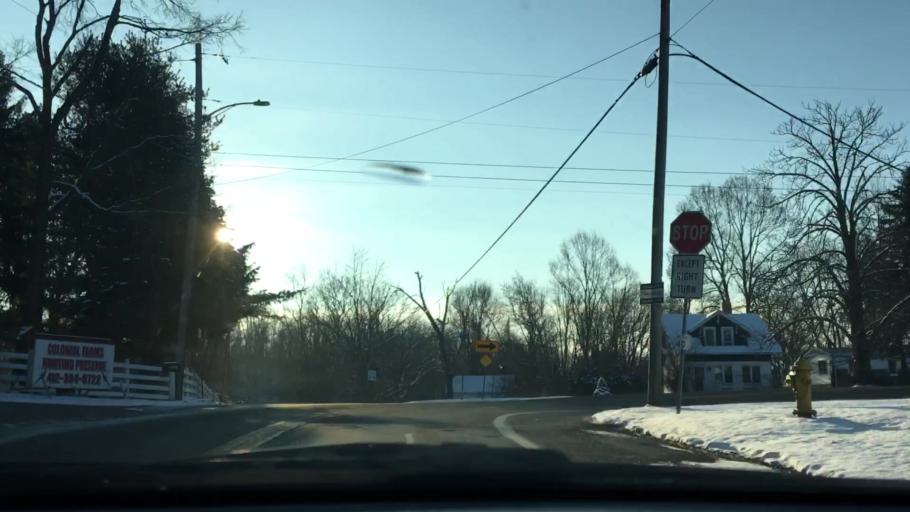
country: US
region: Pennsylvania
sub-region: Allegheny County
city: Elizabeth
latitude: 40.2560
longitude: -79.8457
